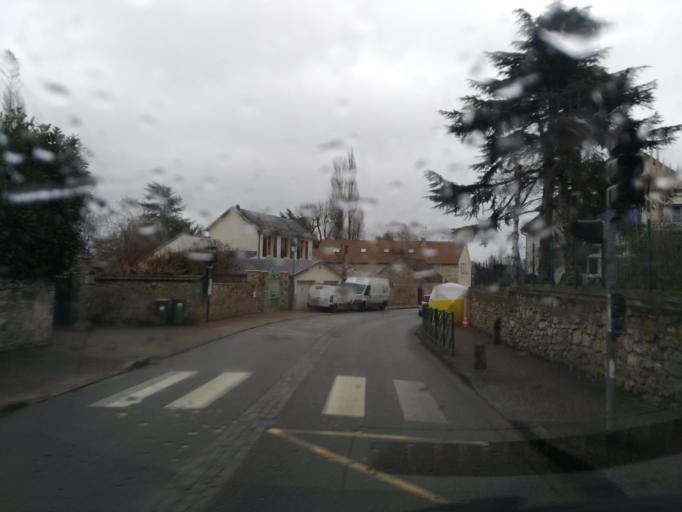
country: FR
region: Ile-de-France
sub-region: Departement des Yvelines
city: Thoiry
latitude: 48.8599
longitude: 1.8191
